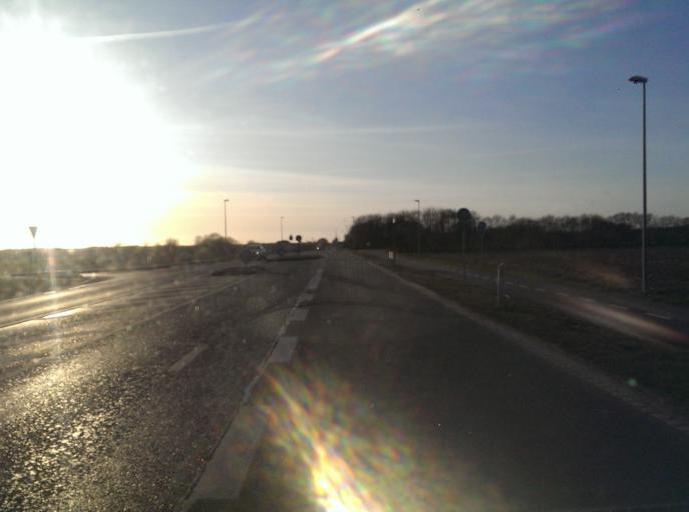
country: DK
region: South Denmark
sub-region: Esbjerg Kommune
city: Esbjerg
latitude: 55.5293
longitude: 8.4195
